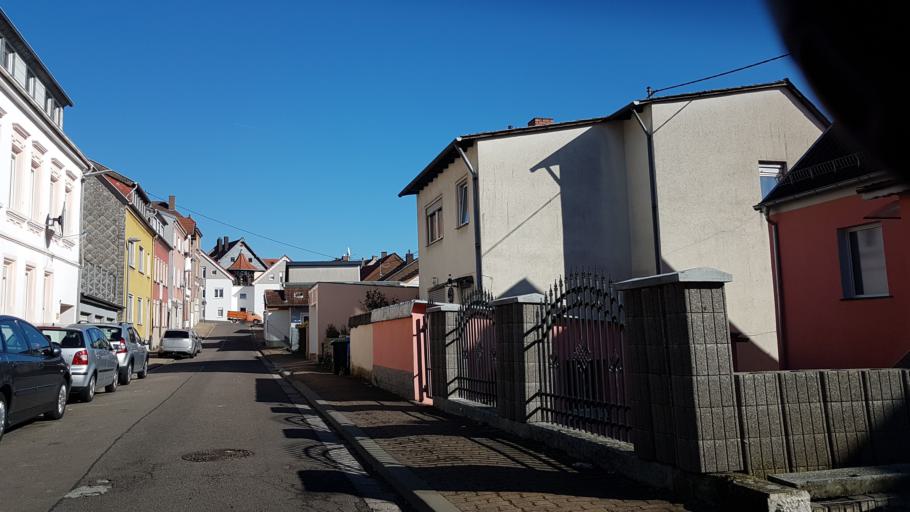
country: DE
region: Saarland
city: Sulzbach
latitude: 49.3004
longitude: 7.0617
